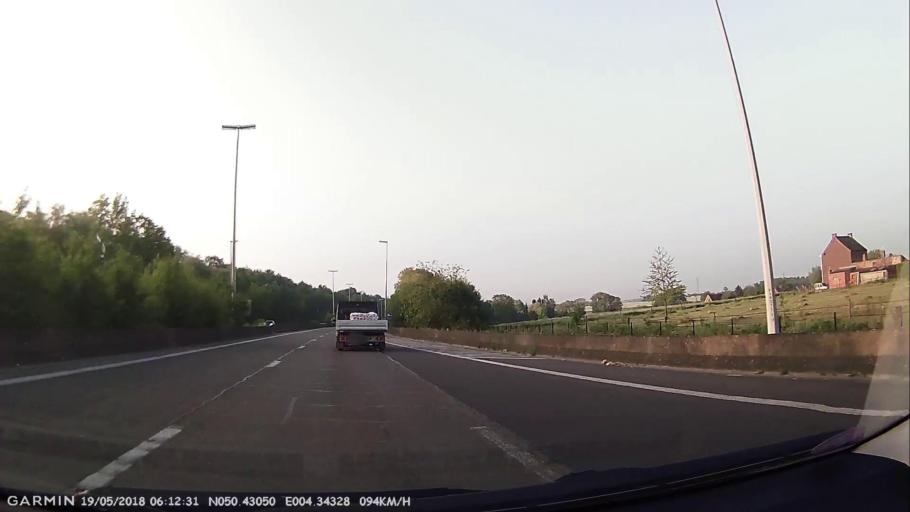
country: BE
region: Wallonia
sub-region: Province du Hainaut
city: Courcelles
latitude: 50.4303
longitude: 4.3434
